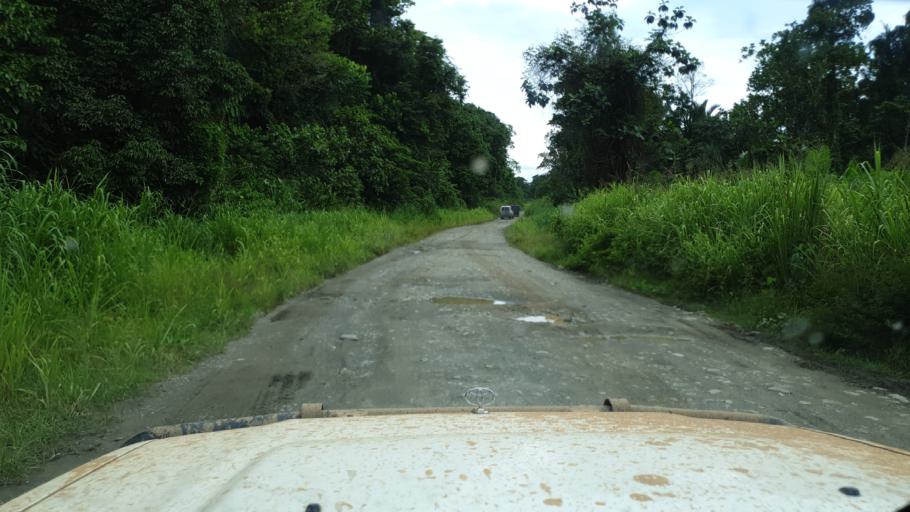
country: PG
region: Northern Province
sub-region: Sohe
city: Kokoda
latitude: -8.9162
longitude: 147.8528
